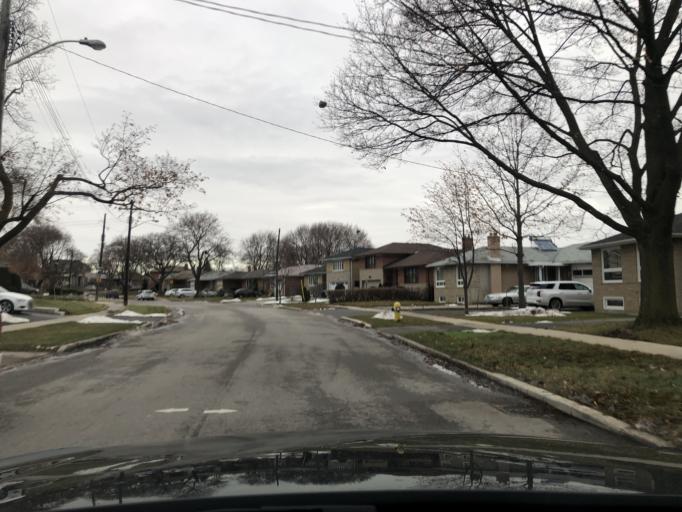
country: CA
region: Ontario
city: Etobicoke
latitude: 43.6905
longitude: -79.5321
